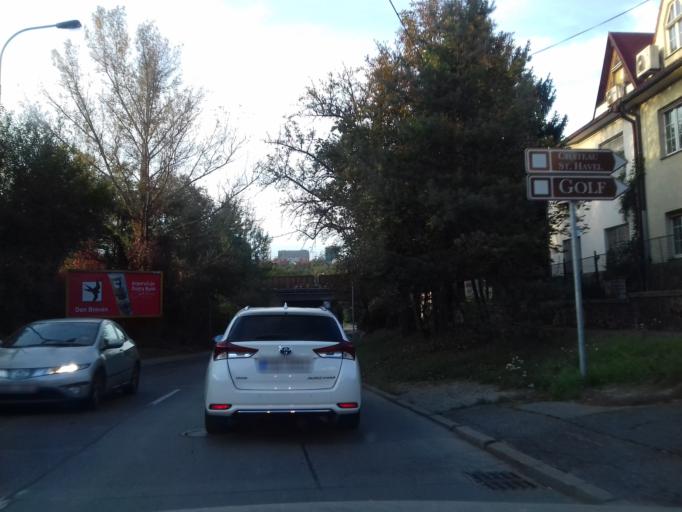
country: CZ
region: Praha
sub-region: Praha 4
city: Hodkovicky
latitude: 50.0325
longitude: 14.4445
